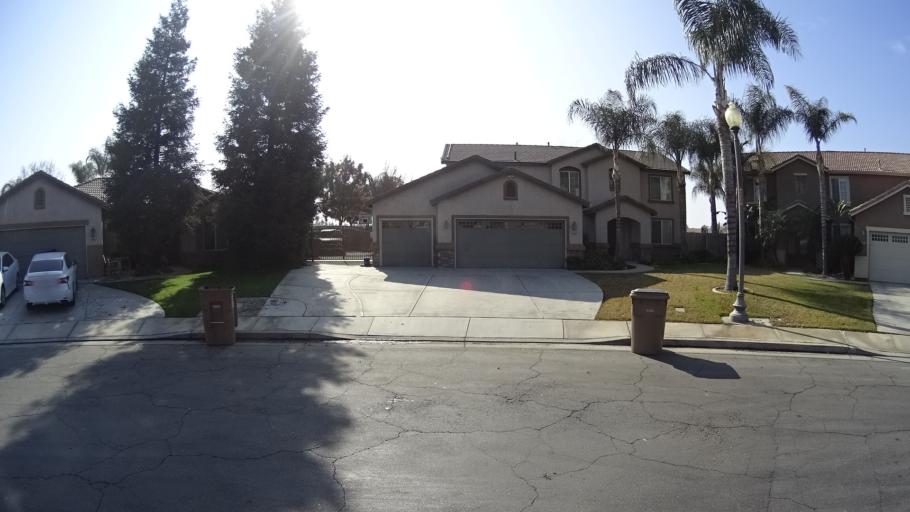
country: US
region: California
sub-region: Kern County
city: Greenacres
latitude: 35.4231
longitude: -119.1187
